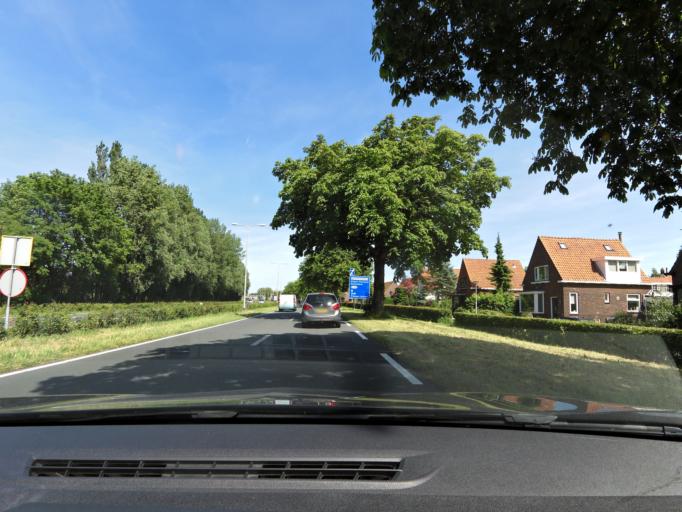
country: NL
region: South Holland
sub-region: Gemeente Albrandswaard
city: Rhoon
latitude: 51.8578
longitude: 4.4113
